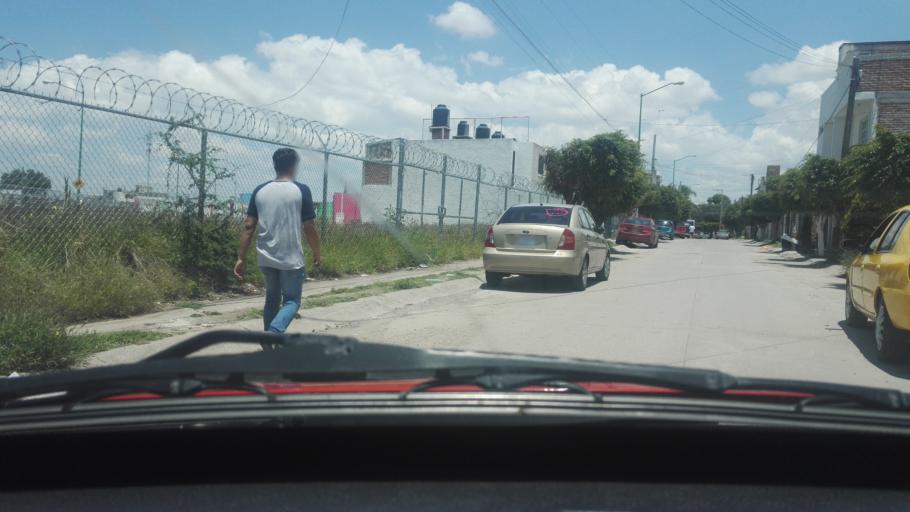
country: MX
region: Guanajuato
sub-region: Leon
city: San Jose de Duran (Los Troncoso)
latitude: 21.0779
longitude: -101.6394
